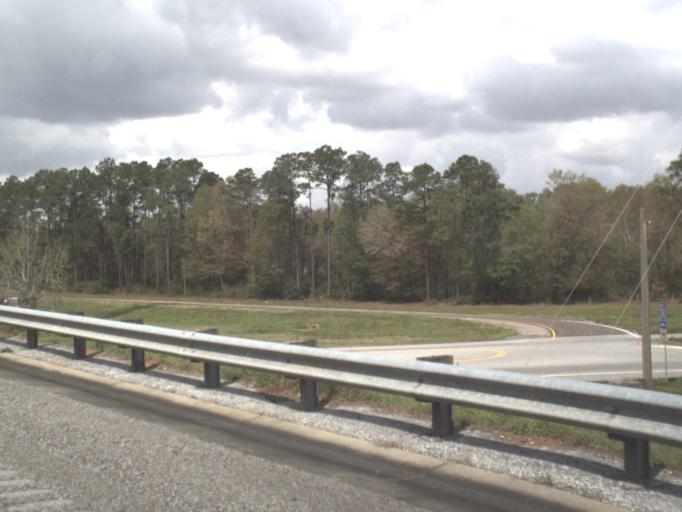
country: US
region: Florida
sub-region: Okaloosa County
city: Crestview
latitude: 30.6991
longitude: -86.7507
